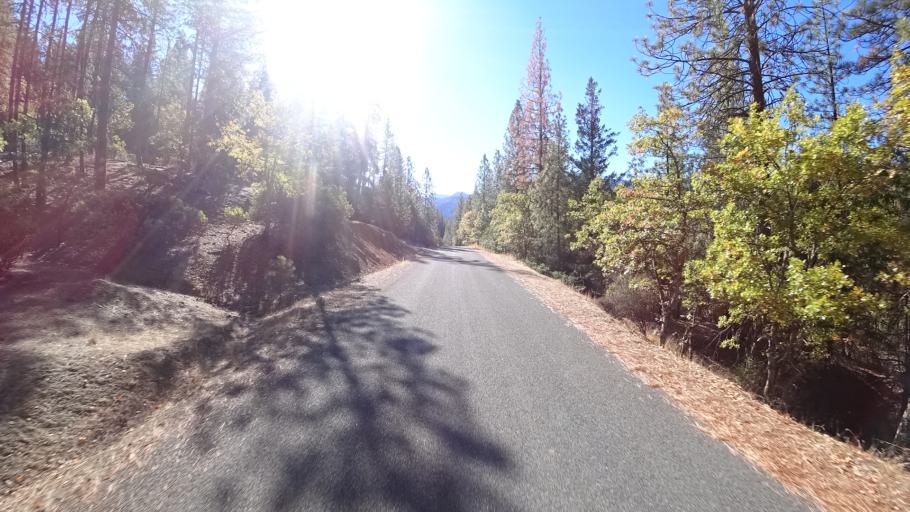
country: US
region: California
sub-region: Trinity County
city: Weaverville
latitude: 41.1287
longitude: -123.0950
